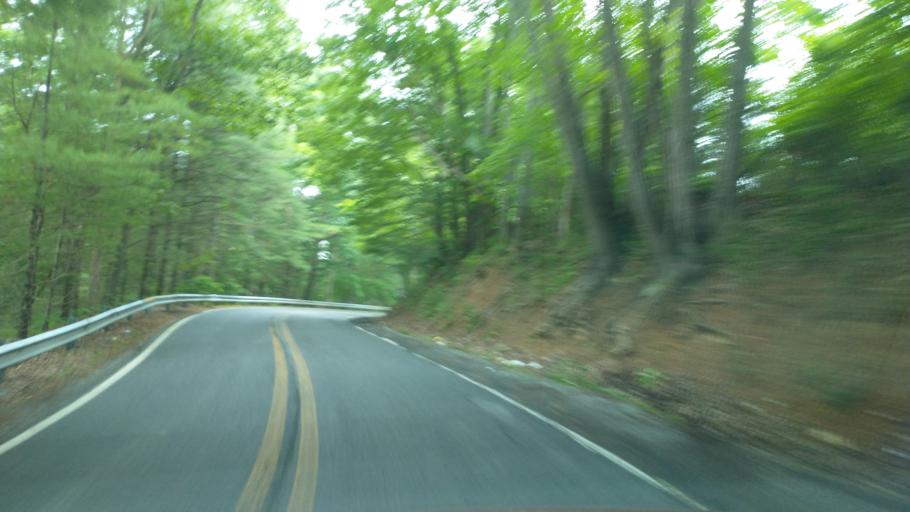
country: US
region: West Virginia
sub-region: Mercer County
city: Athens
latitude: 37.4079
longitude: -81.0352
